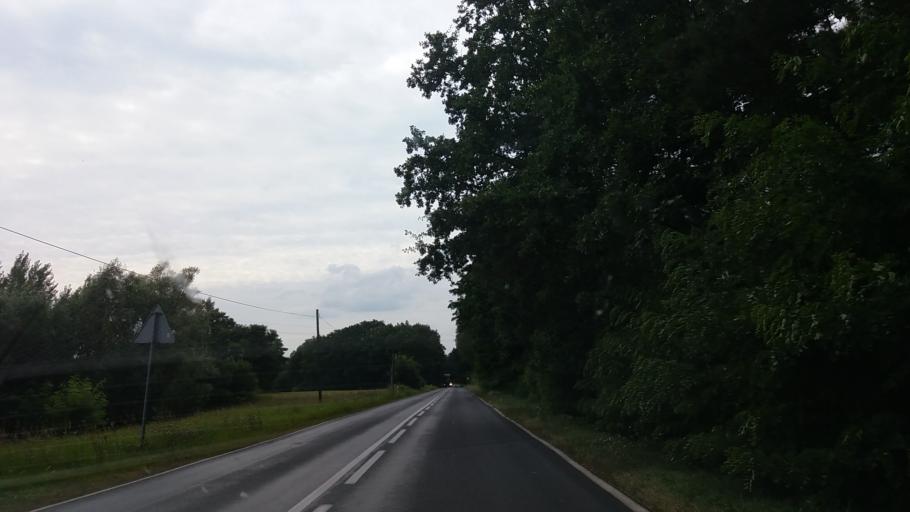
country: PL
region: Lubusz
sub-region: Powiat miedzyrzecki
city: Skwierzyna
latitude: 52.6505
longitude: 15.4610
